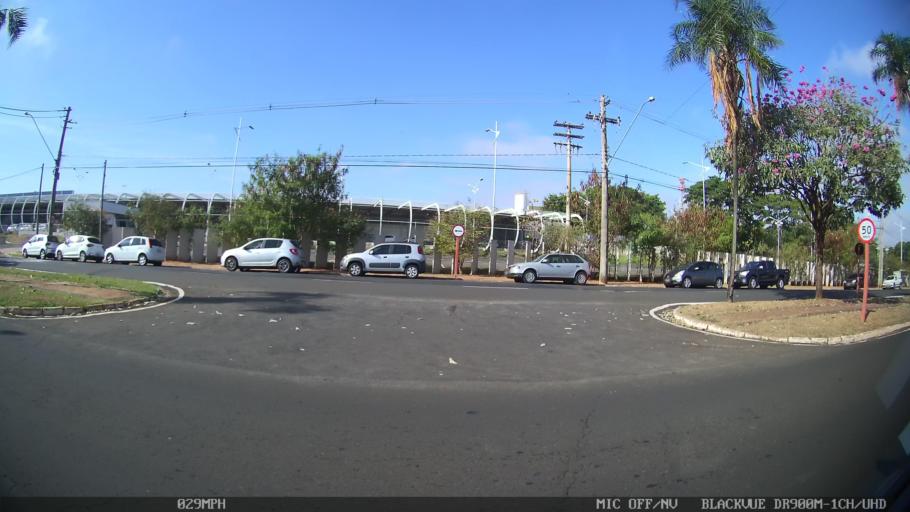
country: BR
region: Sao Paulo
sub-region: Sao Jose Do Rio Preto
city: Sao Jose do Rio Preto
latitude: -20.8125
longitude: -49.4064
